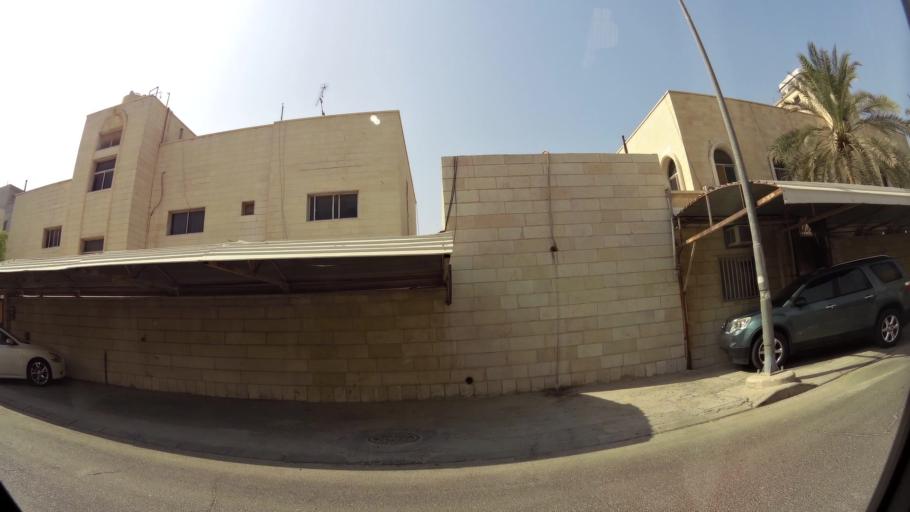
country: KW
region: Al Asimah
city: Ad Dasmah
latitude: 29.3615
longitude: 48.0154
